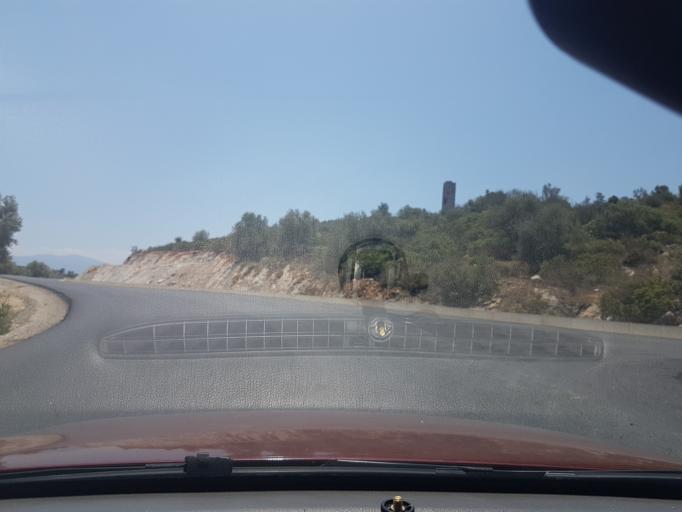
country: GR
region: Central Greece
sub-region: Nomos Evvoias
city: Filla
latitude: 38.4471
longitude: 23.6731
